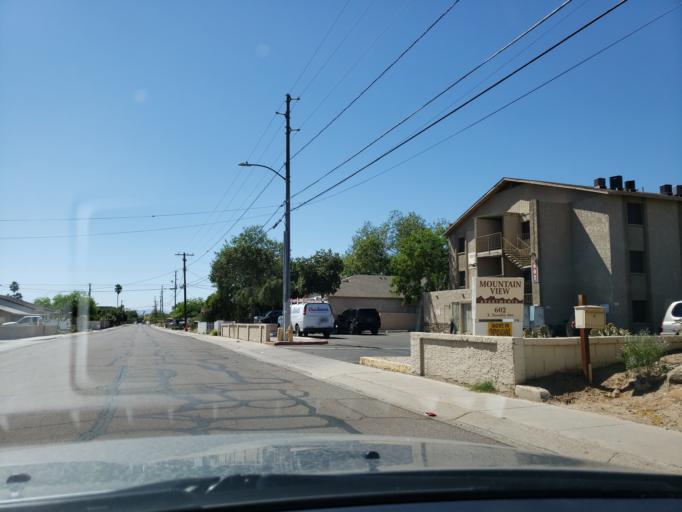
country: US
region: Arizona
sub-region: Maricopa County
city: Phoenix
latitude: 33.5660
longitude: -112.0667
